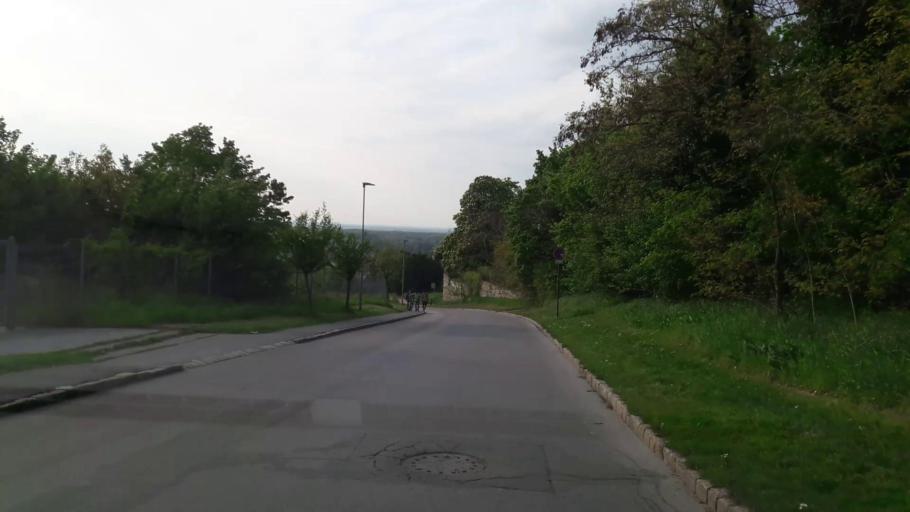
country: AT
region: Lower Austria
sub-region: Politischer Bezirk Bruck an der Leitha
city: Hainburg an der Donau
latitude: 48.1417
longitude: 16.9450
